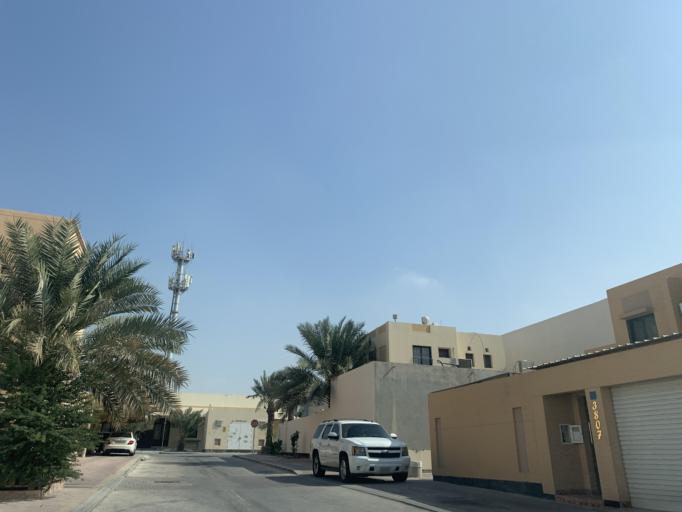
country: BH
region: Central Governorate
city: Madinat Hamad
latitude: 26.1158
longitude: 50.4919
